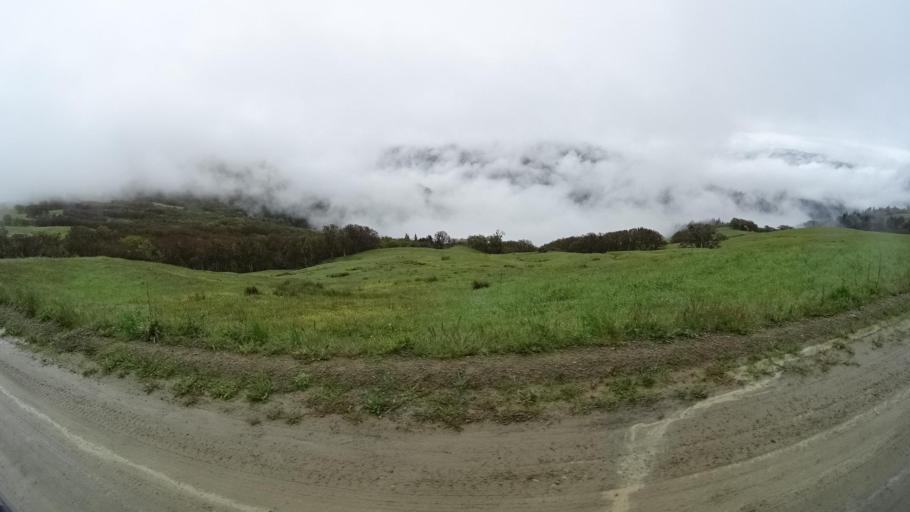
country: US
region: California
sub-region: Humboldt County
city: Westhaven-Moonstone
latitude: 41.1466
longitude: -123.8862
